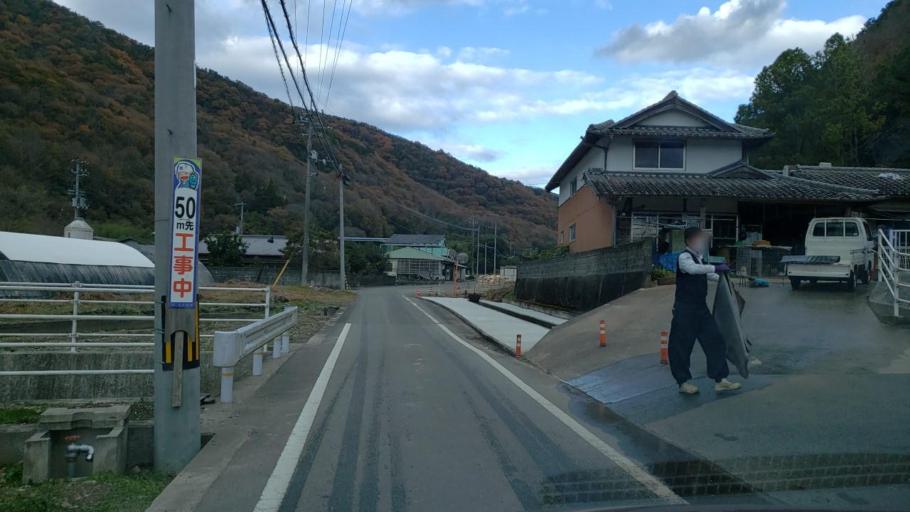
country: JP
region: Tokushima
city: Wakimachi
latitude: 34.1076
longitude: 134.2242
